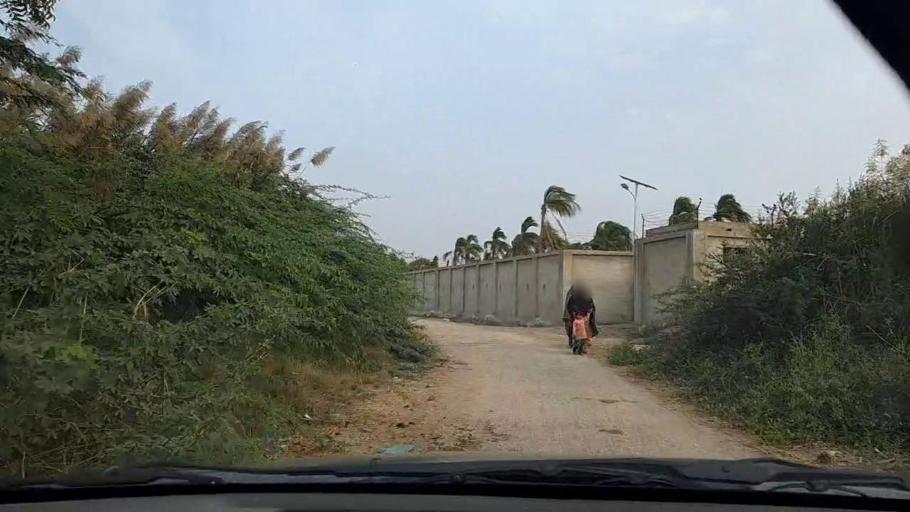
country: PK
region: Sindh
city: Thatta
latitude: 24.7332
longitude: 67.9350
